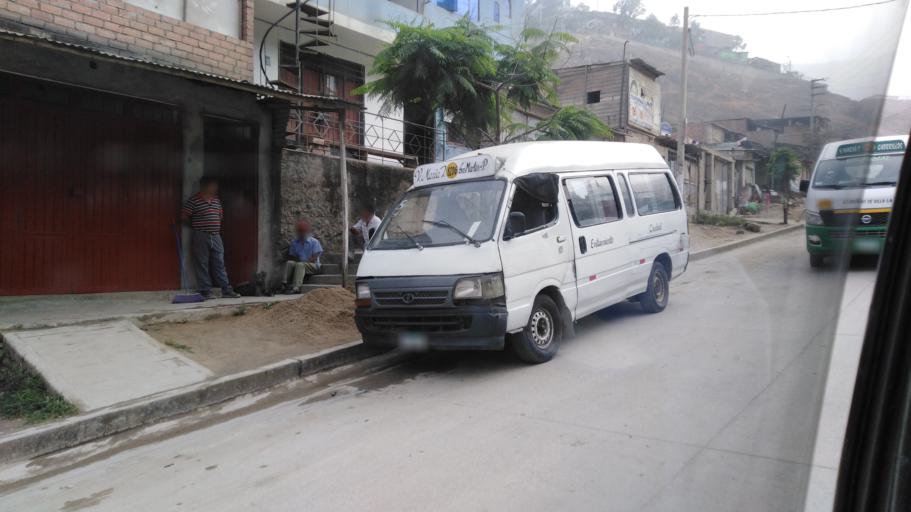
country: PE
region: Lima
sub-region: Lima
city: La Molina
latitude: -12.1470
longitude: -76.9299
